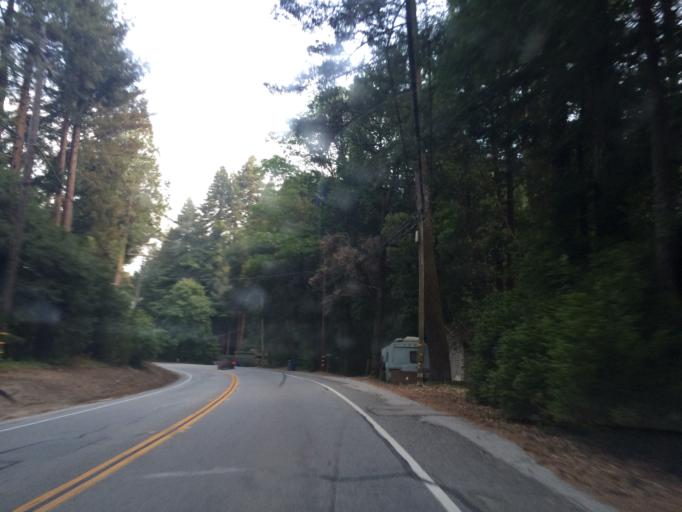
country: US
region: California
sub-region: Santa Cruz County
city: Boulder Creek
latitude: 37.1362
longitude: -122.1277
